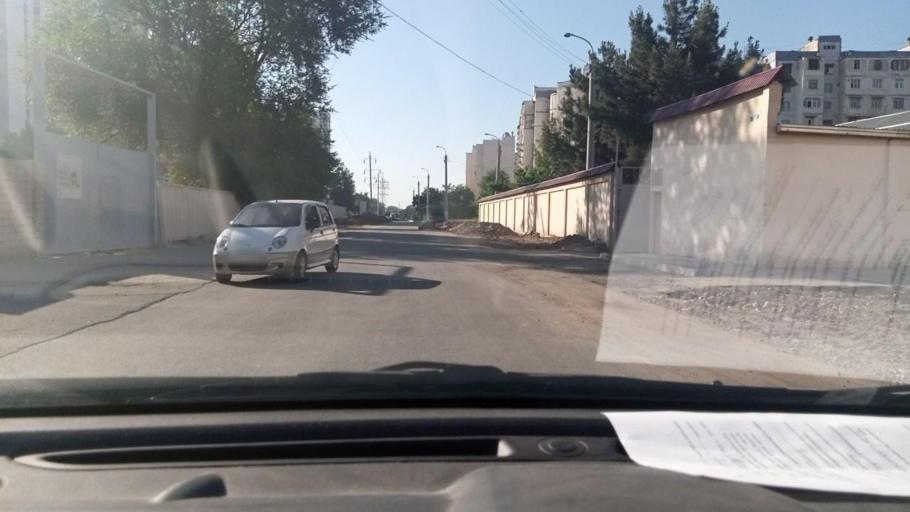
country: UZ
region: Toshkent
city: Salor
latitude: 41.3233
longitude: 69.3577
